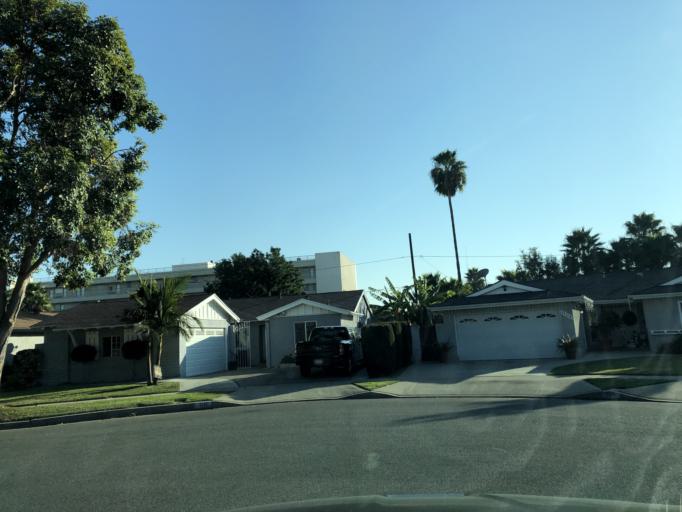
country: US
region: California
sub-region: Orange County
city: Santa Ana
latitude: 33.7634
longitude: -117.8554
